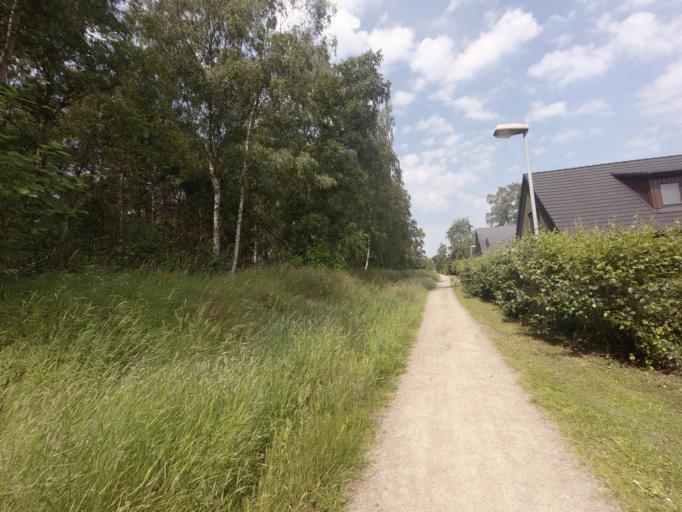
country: SE
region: Skane
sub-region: Vellinge Kommun
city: Skanor med Falsterbo
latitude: 55.4039
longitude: 12.8547
